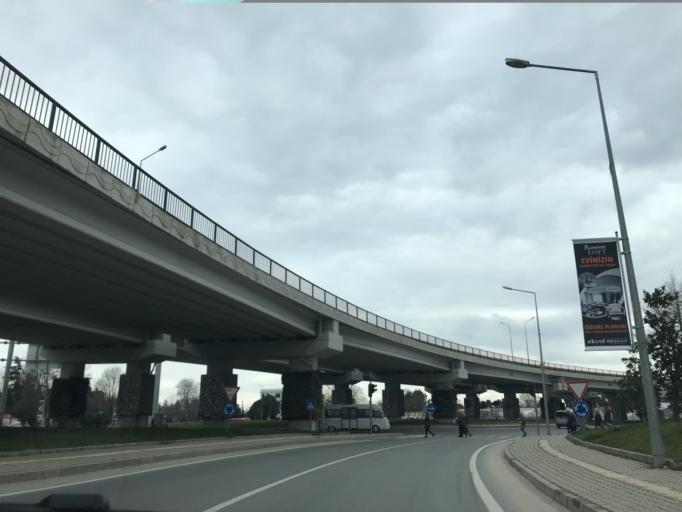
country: TR
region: Yalova
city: Yalova
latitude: 40.6556
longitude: 29.2843
